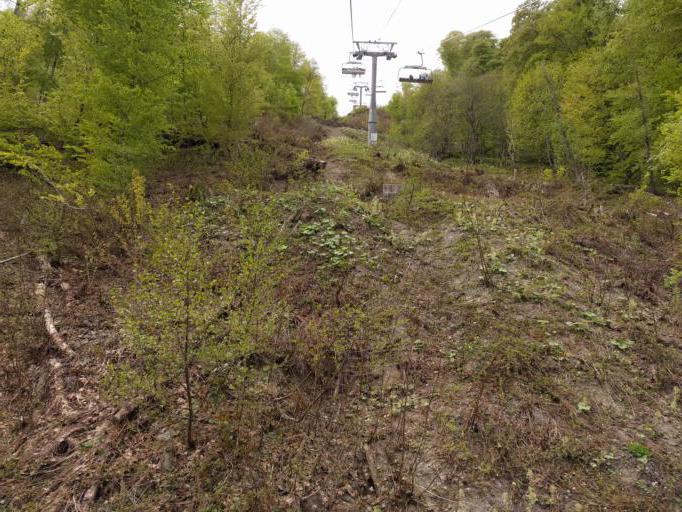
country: RU
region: Krasnodarskiy
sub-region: Sochi City
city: Krasnaya Polyana
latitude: 43.6460
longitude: 40.3264
